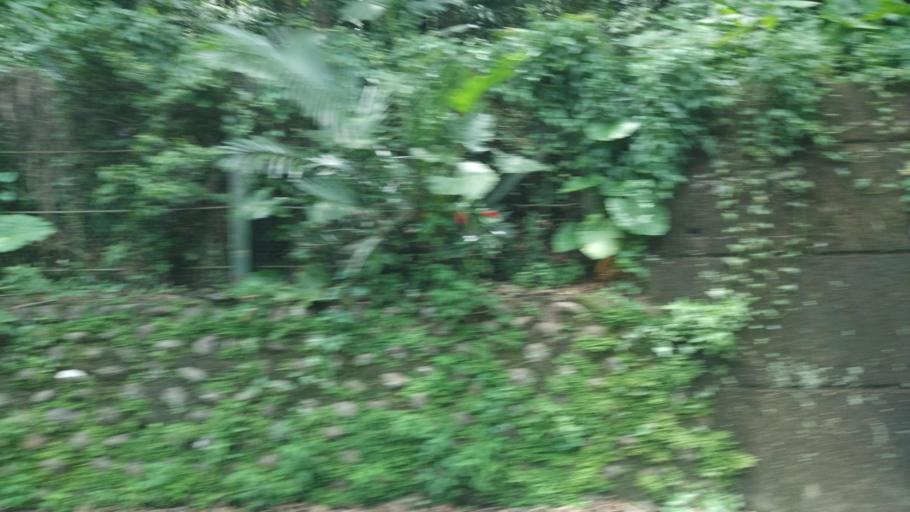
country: TW
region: Taipei
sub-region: Taipei
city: Banqiao
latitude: 24.9267
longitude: 121.4396
